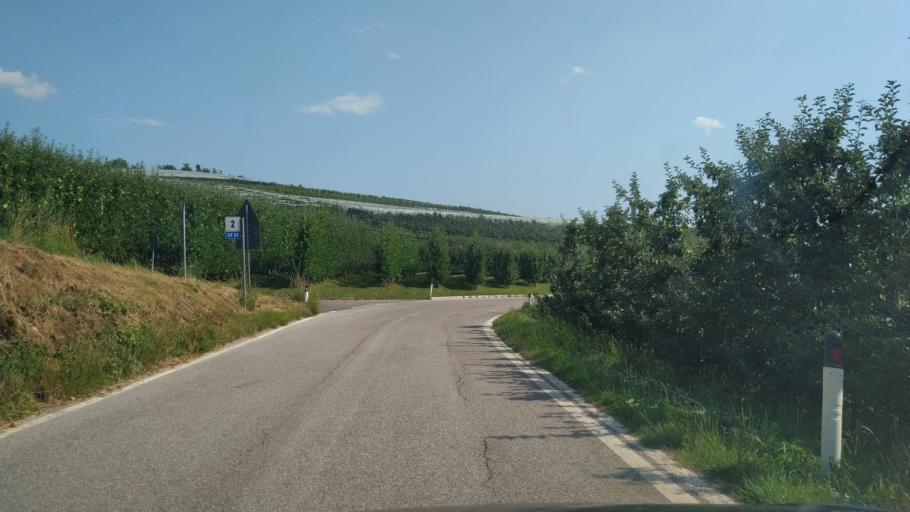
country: IT
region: Trentino-Alto Adige
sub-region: Provincia di Trento
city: Sanzeno
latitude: 46.3841
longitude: 11.0798
